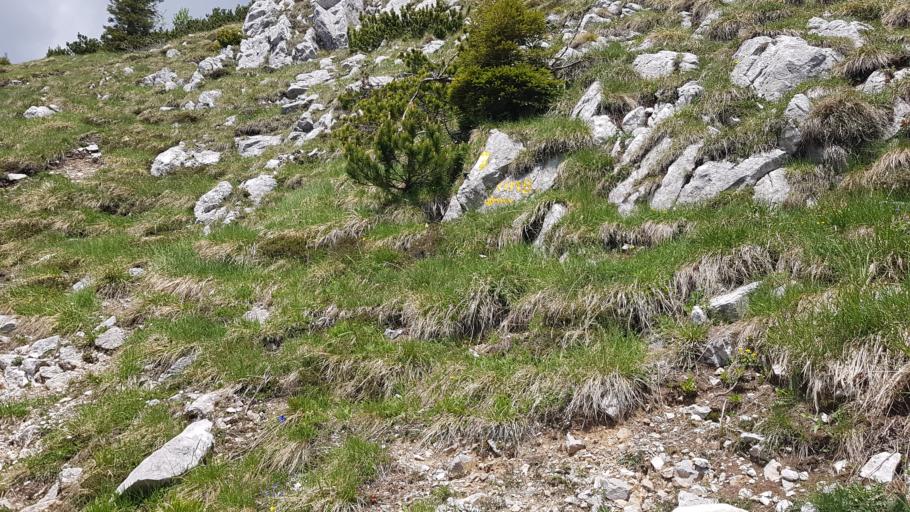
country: IT
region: Friuli Venezia Giulia
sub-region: Provincia di Udine
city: Paularo
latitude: 46.5361
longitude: 13.1805
